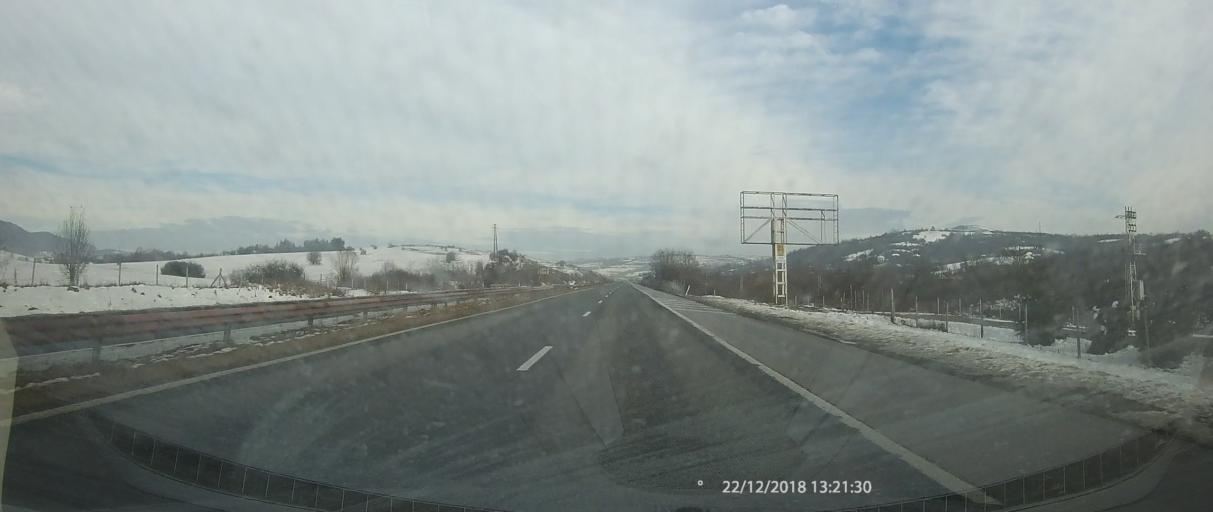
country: BG
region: Lovech
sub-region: Obshtina Yablanitsa
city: Yablanitsa
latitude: 42.9769
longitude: 24.0420
